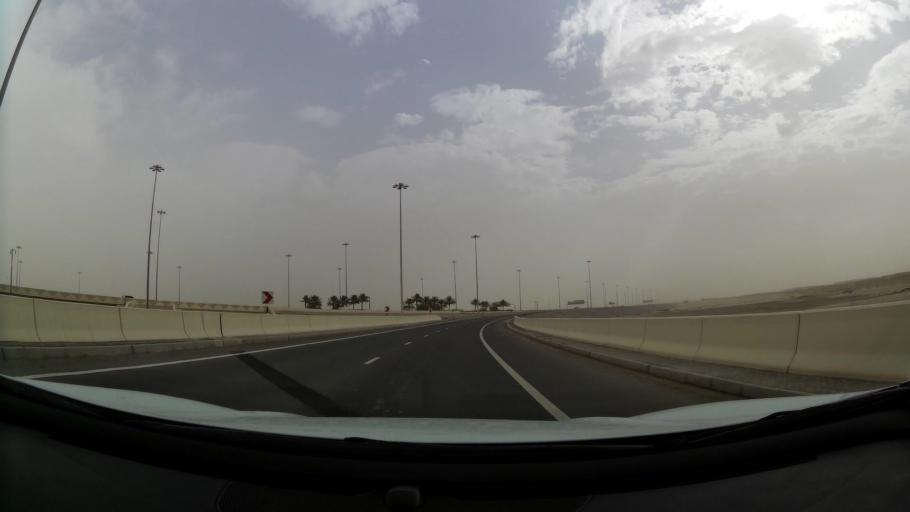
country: AE
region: Abu Dhabi
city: Abu Dhabi
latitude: 24.4826
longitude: 54.6478
